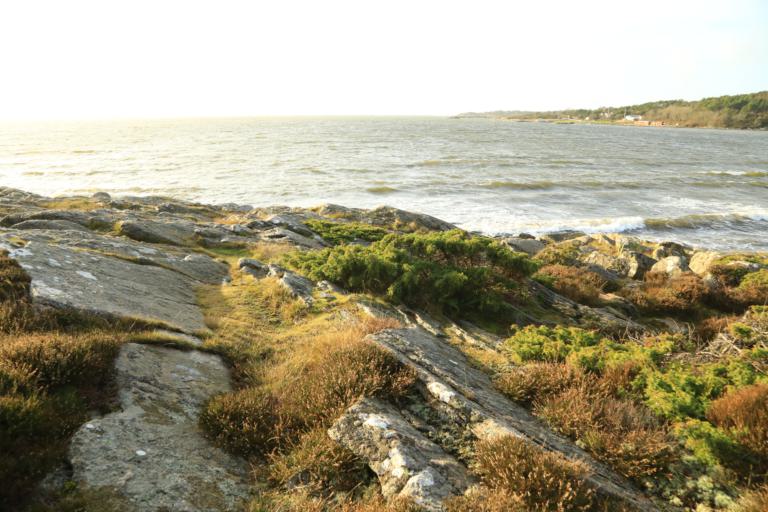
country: SE
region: Halland
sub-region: Varbergs Kommun
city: Varberg
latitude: 57.1878
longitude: 12.2056
